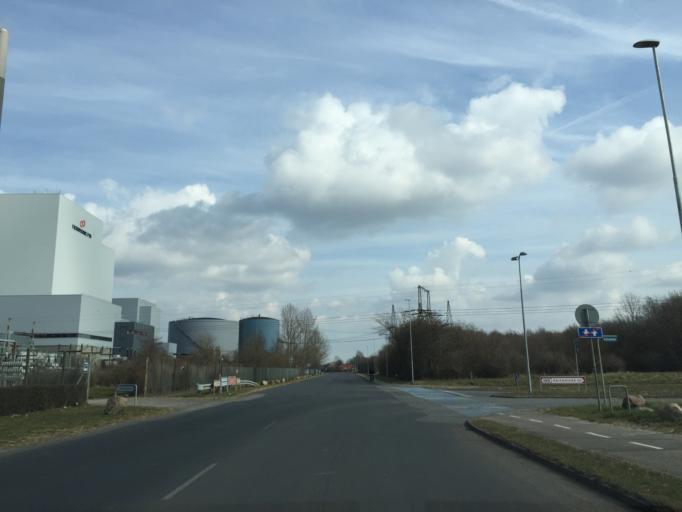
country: DK
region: South Denmark
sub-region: Odense Kommune
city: Stige
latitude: 55.4271
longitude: 10.4061
